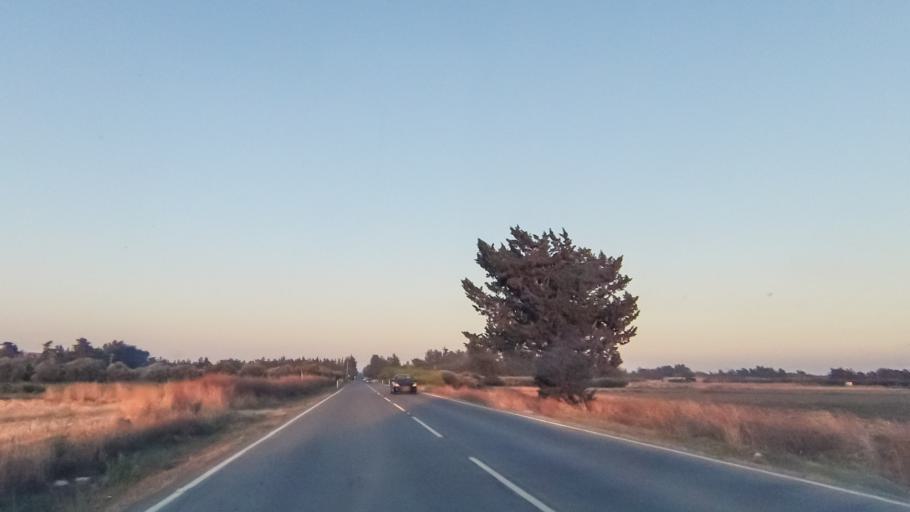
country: CY
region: Limassol
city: Erimi
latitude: 34.6615
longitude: 32.8987
